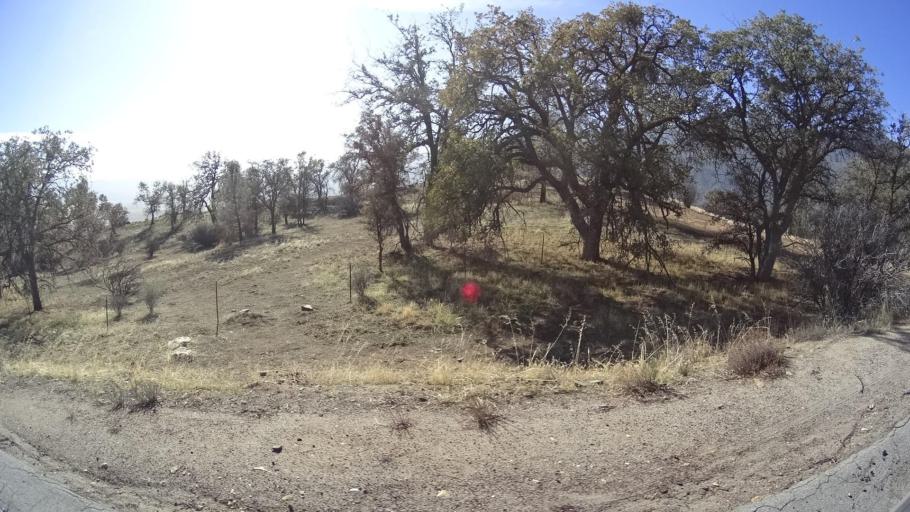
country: US
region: California
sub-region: Kern County
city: Bodfish
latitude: 35.4401
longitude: -118.5303
